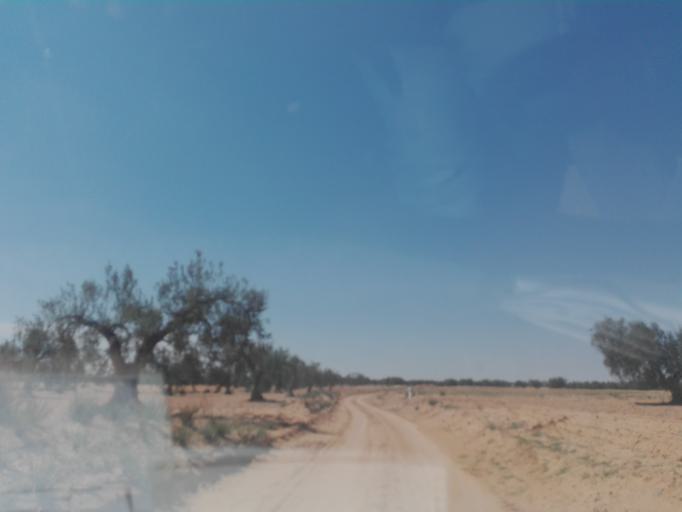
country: TN
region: Safaqis
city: Bi'r `Ali Bin Khalifah
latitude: 34.6066
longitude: 10.3503
